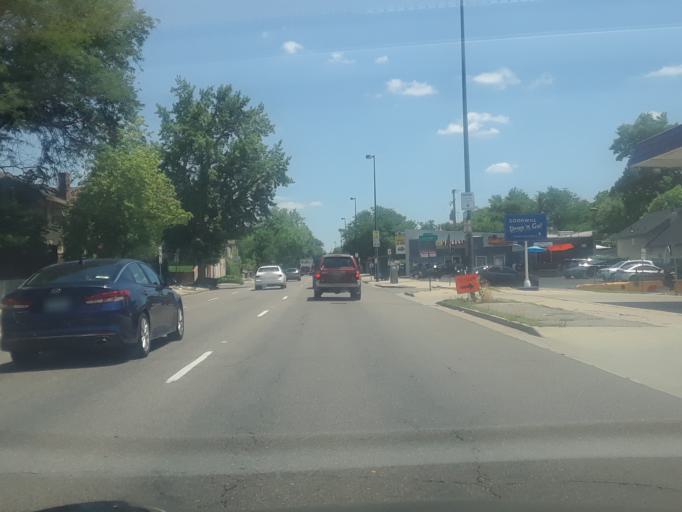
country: US
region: Colorado
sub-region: Arapahoe County
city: Glendale
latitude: 39.7256
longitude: -104.9565
